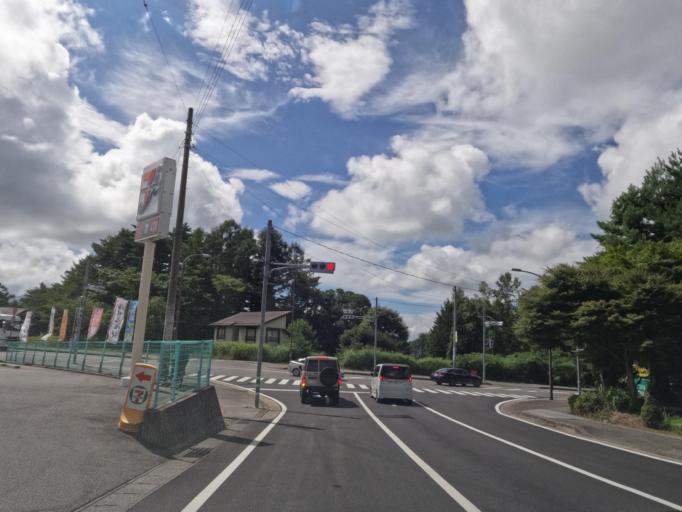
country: JP
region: Yamanashi
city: Nirasaki
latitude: 35.8870
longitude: 138.4115
